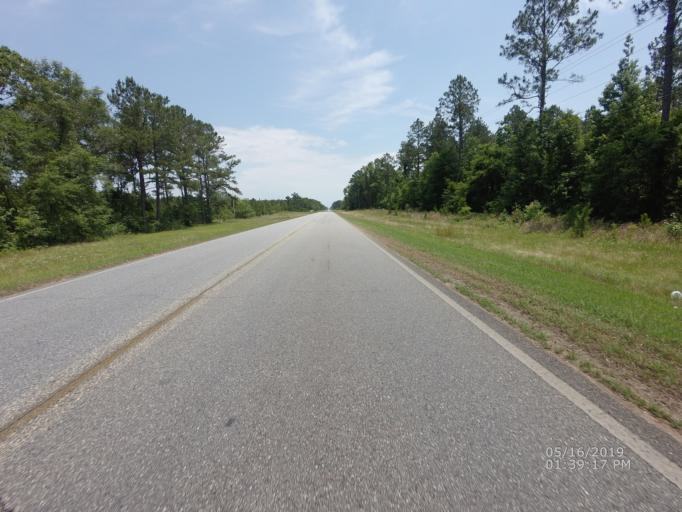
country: US
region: Georgia
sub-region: Dougherty County
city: Albany
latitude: 31.5490
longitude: -84.2446
